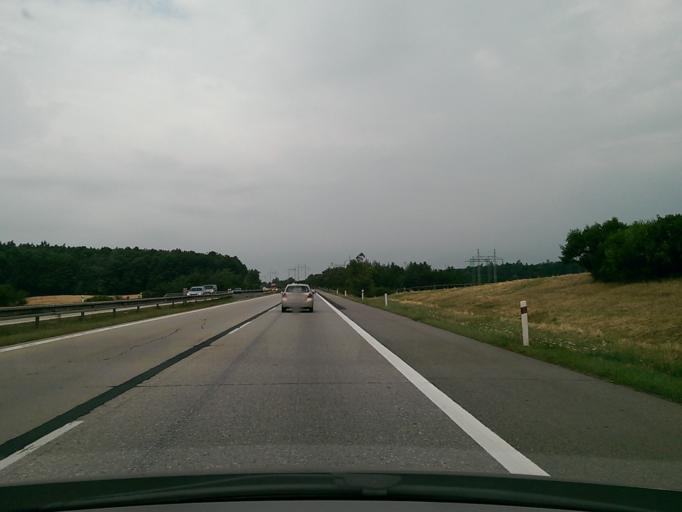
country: CZ
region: South Moravian
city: Ricany
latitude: 49.2397
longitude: 16.3711
